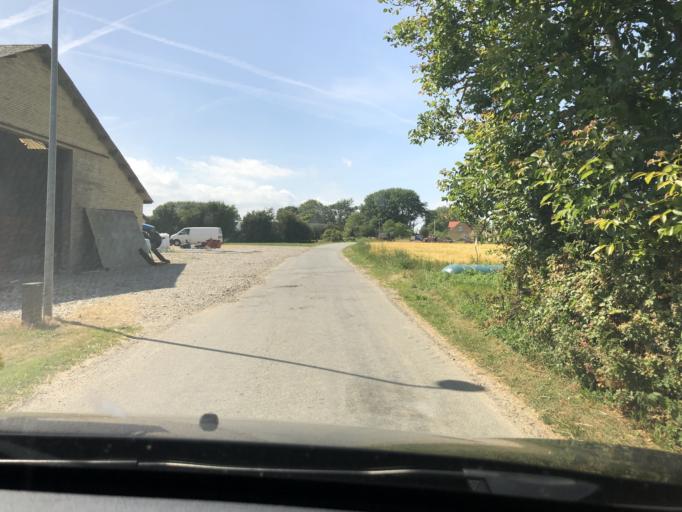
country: DK
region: South Denmark
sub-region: AEro Kommune
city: AEroskobing
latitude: 54.8921
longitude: 10.3010
